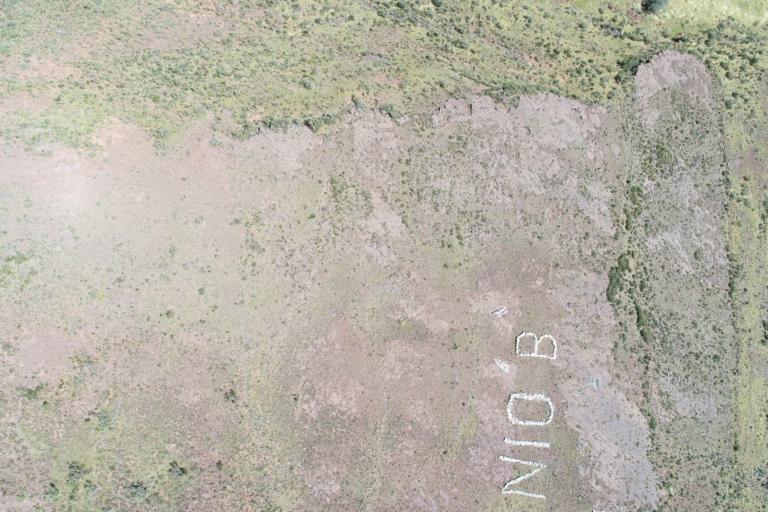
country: BO
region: La Paz
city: Tiahuanaco
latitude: -16.6104
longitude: -68.7626
